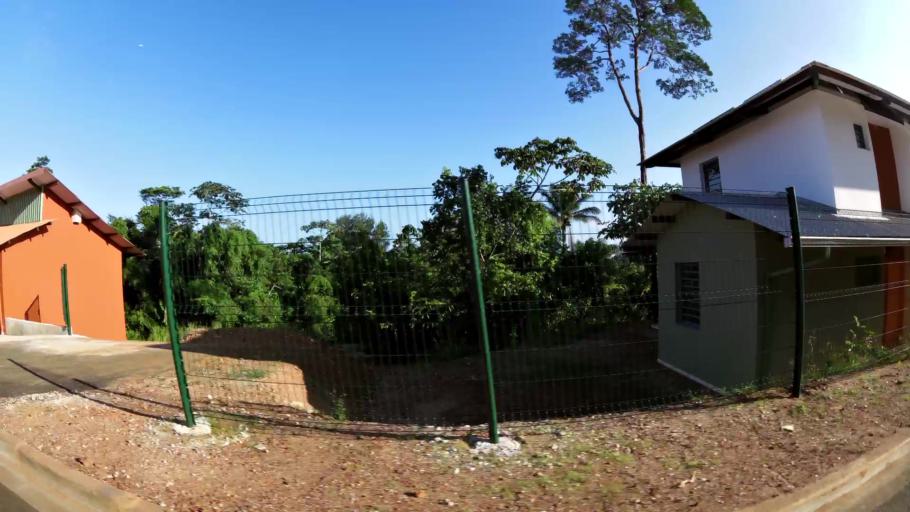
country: GF
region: Guyane
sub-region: Guyane
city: Remire-Montjoly
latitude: 4.8880
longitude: -52.2962
